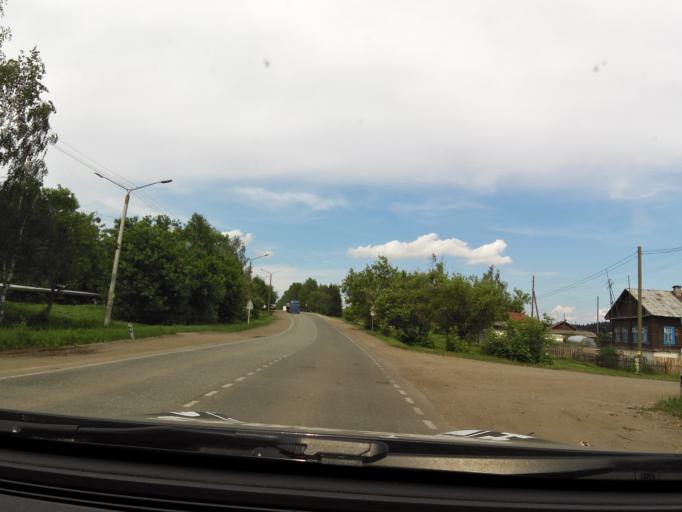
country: RU
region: Kirov
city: Vakhrushi
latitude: 58.6844
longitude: 50.0352
